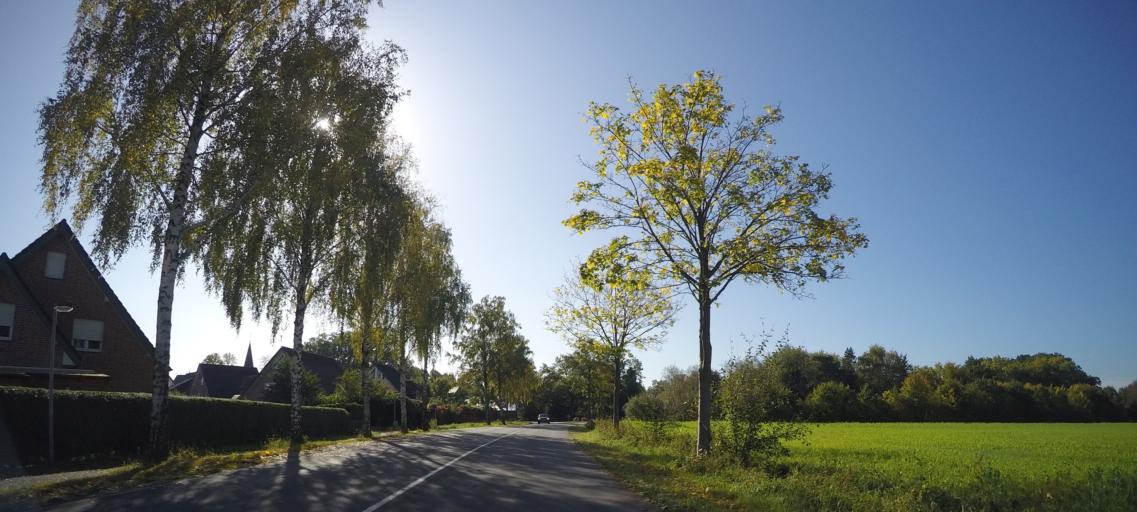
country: DE
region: North Rhine-Westphalia
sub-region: Regierungsbezirk Arnsberg
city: Lippstadt
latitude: 51.6847
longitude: 8.3001
